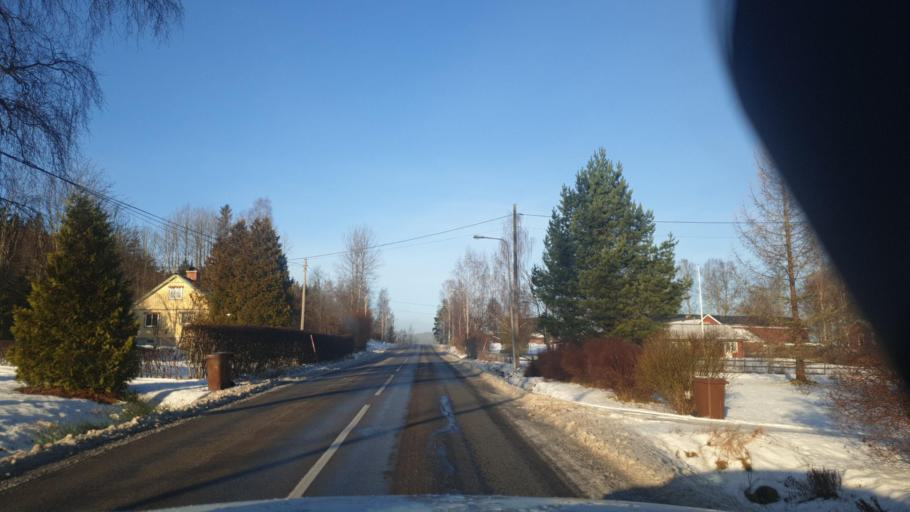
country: SE
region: Vaermland
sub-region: Eda Kommun
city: Amotfors
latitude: 59.6683
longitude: 12.4218
